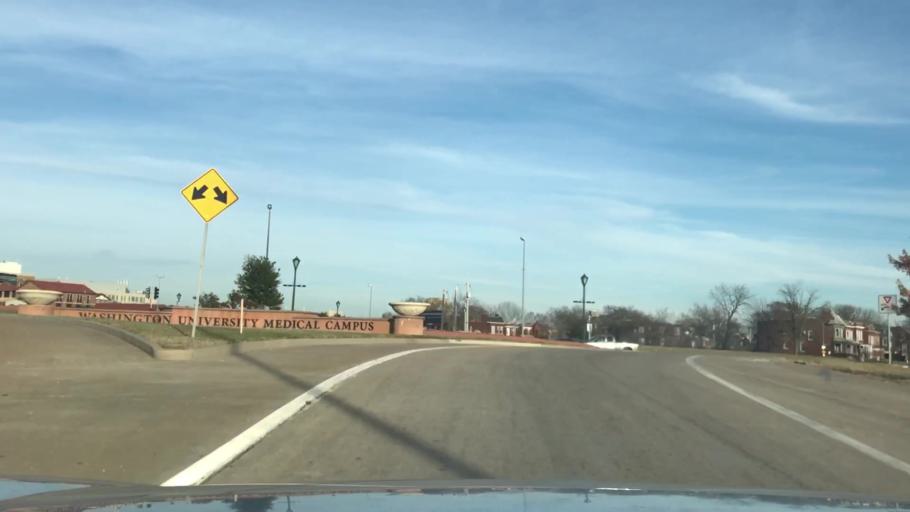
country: US
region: Missouri
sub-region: Saint Louis County
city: University City
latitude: 38.6304
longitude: -90.2660
